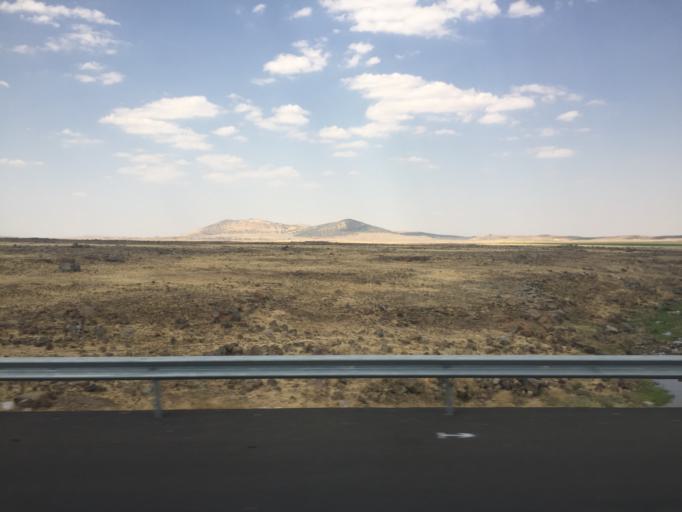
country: TR
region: Sanliurfa
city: Karacadag
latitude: 37.8488
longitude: 39.7139
